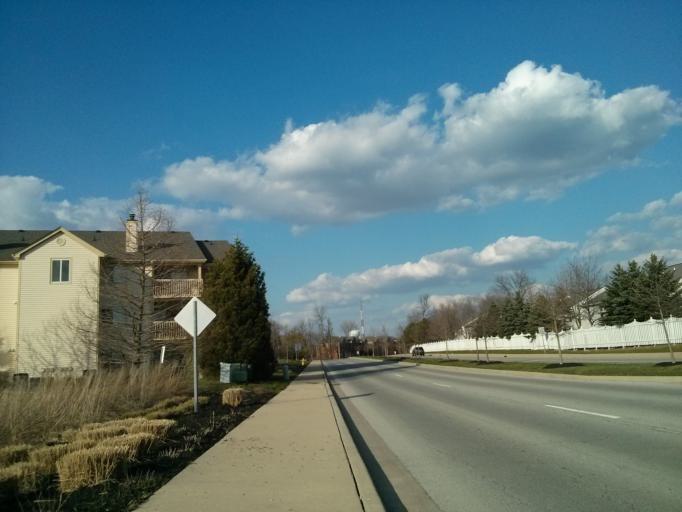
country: US
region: Indiana
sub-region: Hamilton County
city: Carmel
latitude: 39.9689
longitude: -86.1386
